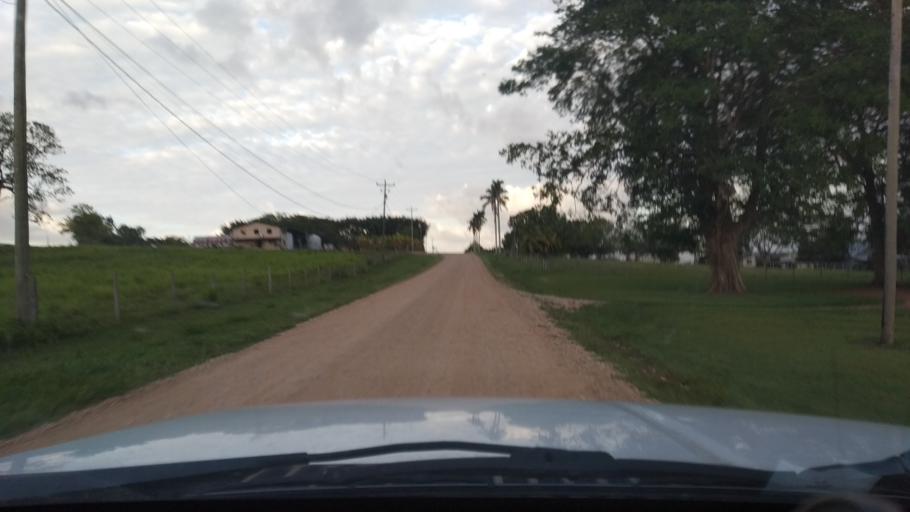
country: BZ
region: Cayo
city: San Ignacio
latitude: 17.2264
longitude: -88.9920
